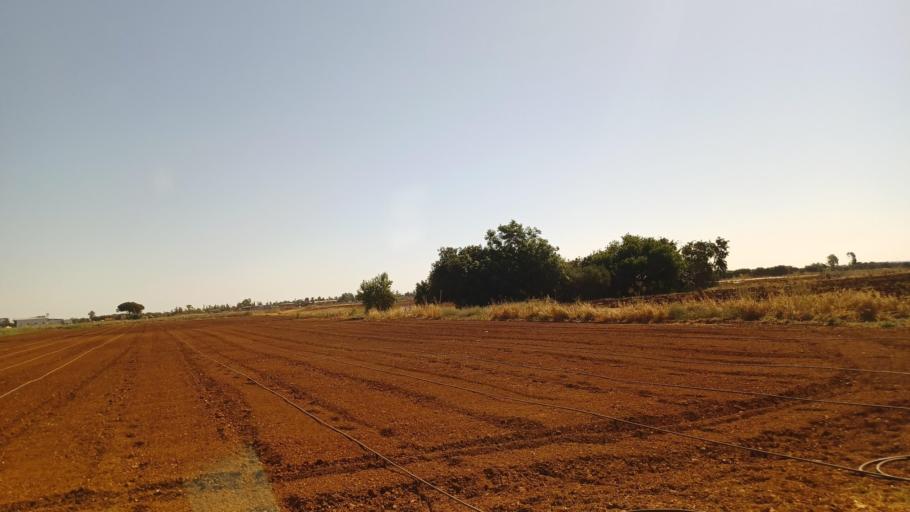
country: CY
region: Ammochostos
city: Avgorou
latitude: 35.0106
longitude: 33.8522
